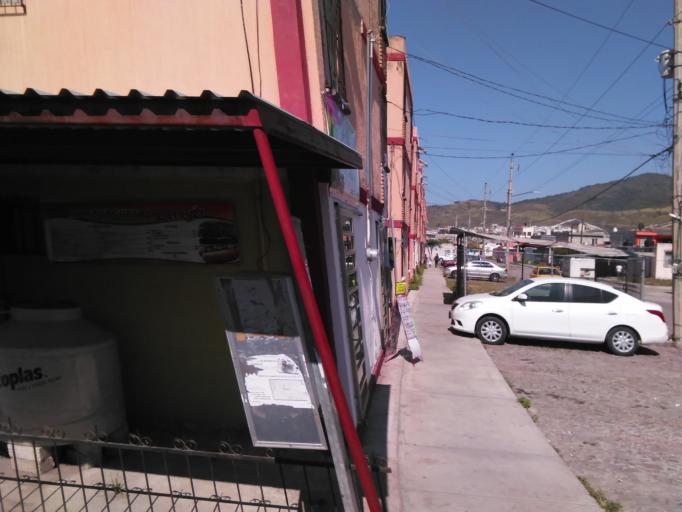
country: MX
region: Nayarit
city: Tepic
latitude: 21.4830
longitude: -104.8530
